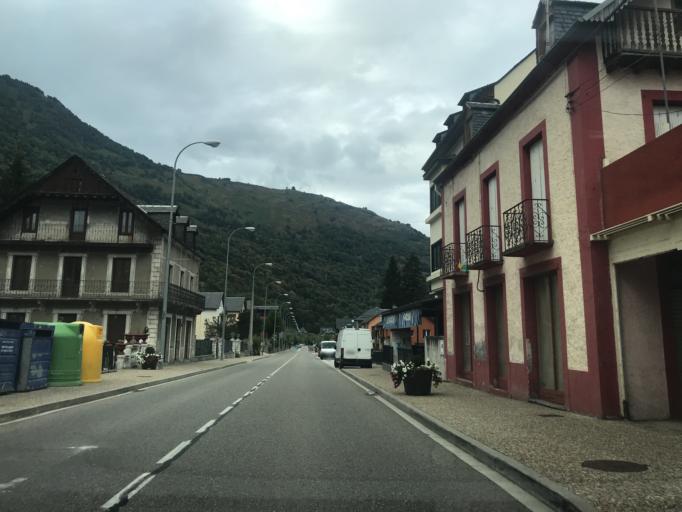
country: ES
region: Catalonia
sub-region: Provincia de Lleida
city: Les
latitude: 42.8112
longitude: 0.7099
